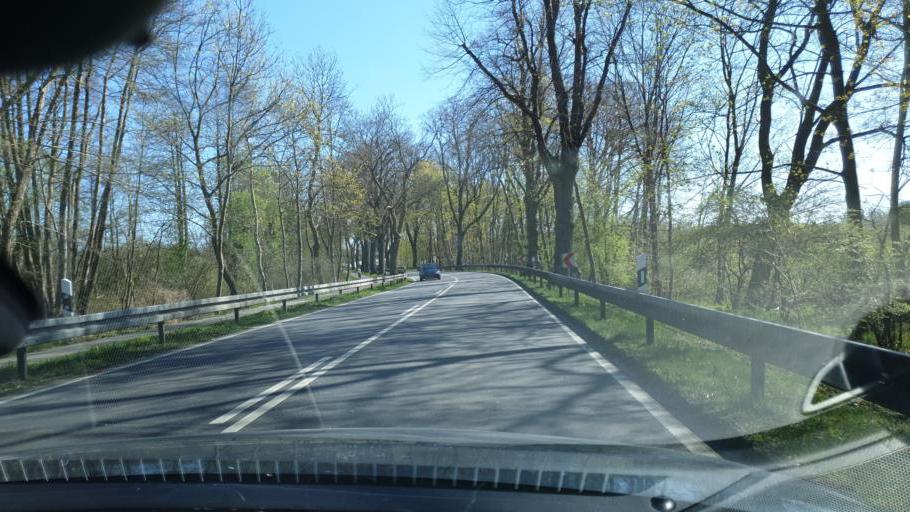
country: DE
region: Mecklenburg-Vorpommern
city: Leezen
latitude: 53.6859
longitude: 11.4743
